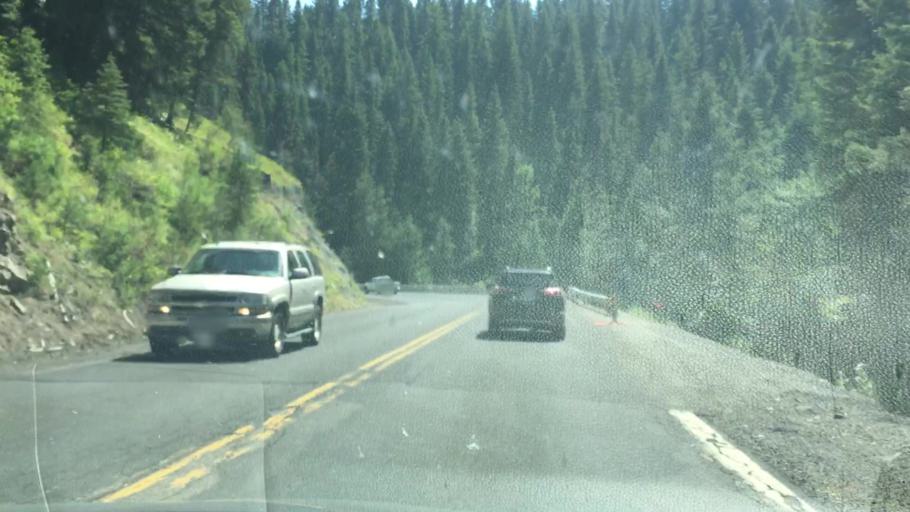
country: US
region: Idaho
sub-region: Valley County
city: McCall
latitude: 44.9621
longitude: -116.1738
